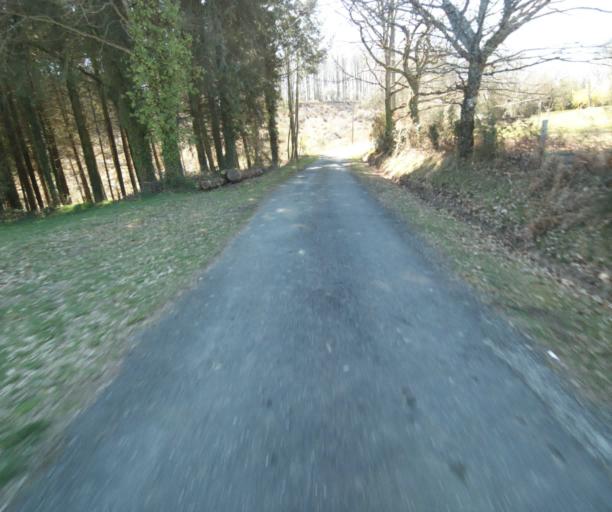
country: FR
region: Limousin
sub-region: Departement de la Correze
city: Saint-Mexant
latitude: 45.2818
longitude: 1.6644
